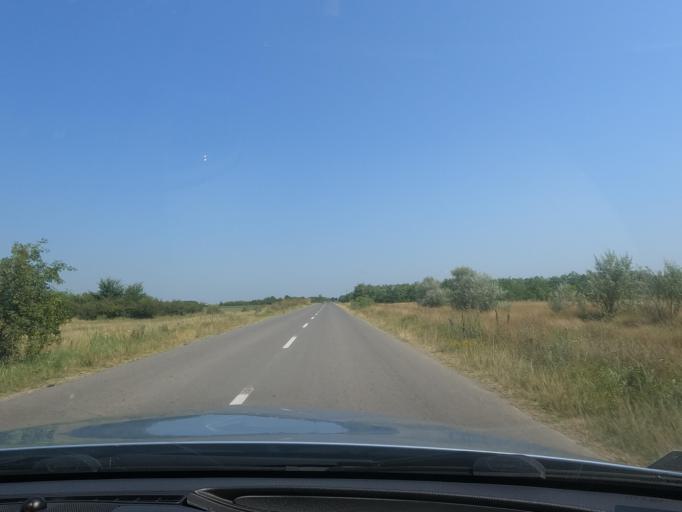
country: RS
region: Autonomna Pokrajina Vojvodina
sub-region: Juznobacki Okrug
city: Kovilj
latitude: 45.2205
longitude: 20.0502
